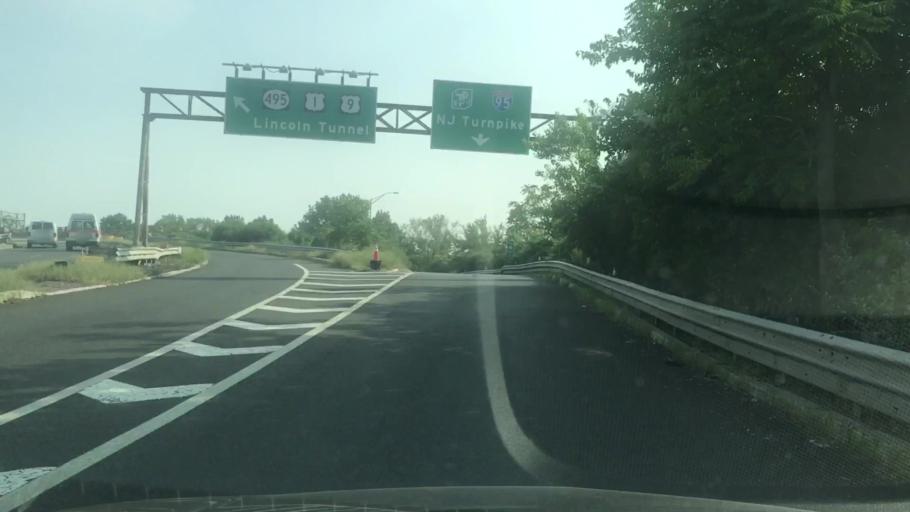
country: US
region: New Jersey
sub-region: Hudson County
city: Secaucus
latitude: 40.7815
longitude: -74.0478
